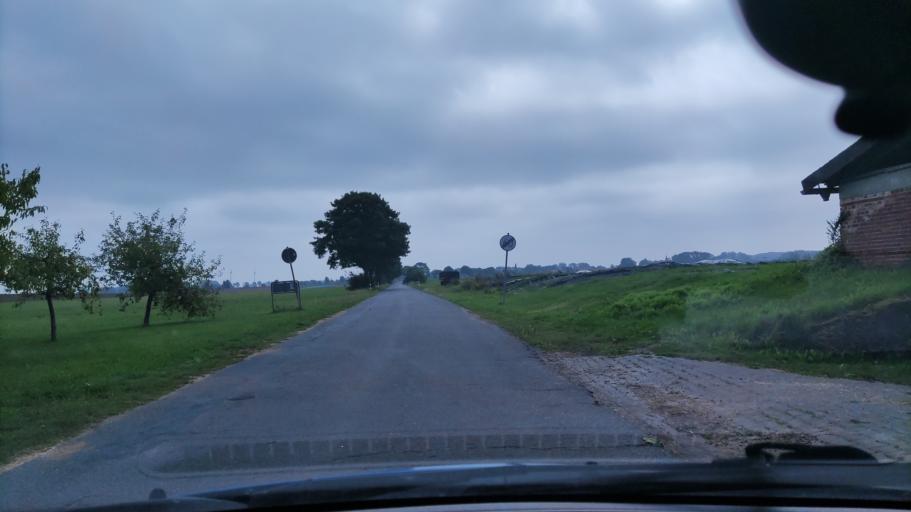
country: DE
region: Lower Saxony
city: Altenmedingen
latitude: 53.1399
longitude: 10.5926
